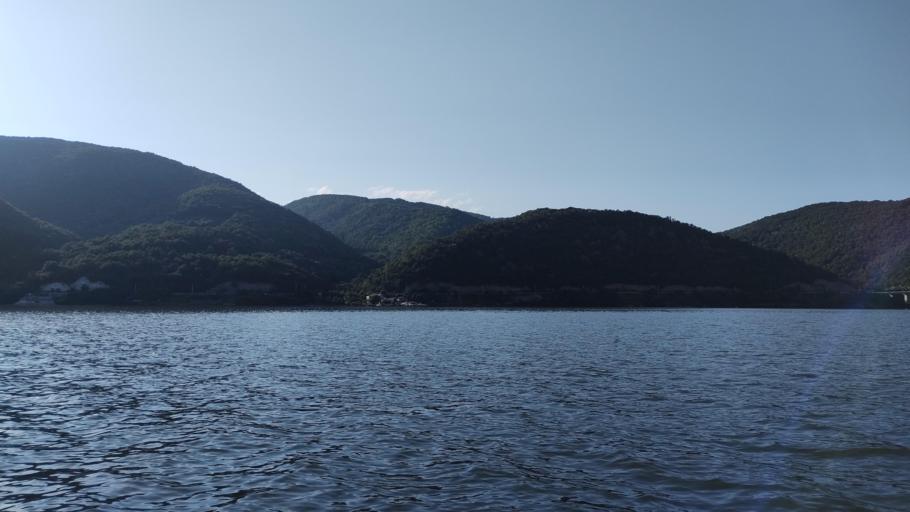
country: RO
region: Mehedinti
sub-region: Comuna Dubova
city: Dubova
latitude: 44.5767
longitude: 22.2455
